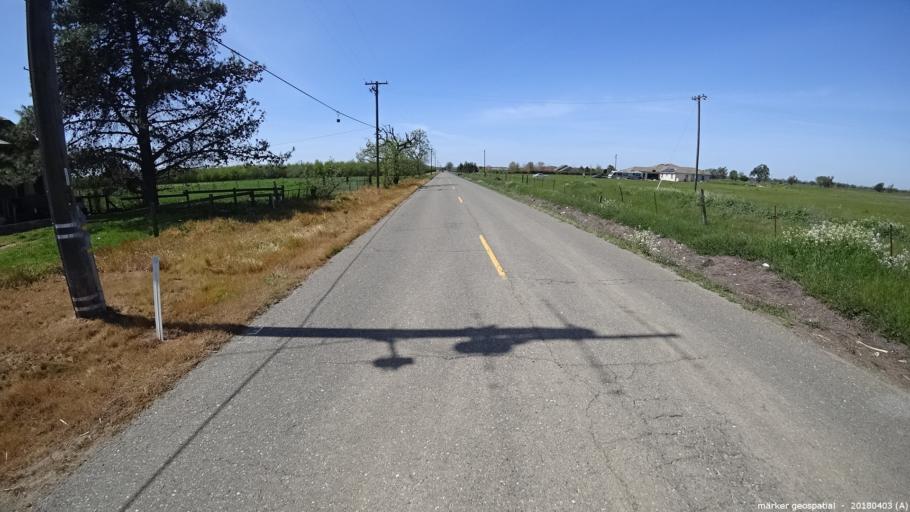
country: US
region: California
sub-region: Sacramento County
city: Wilton
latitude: 38.3799
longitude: -121.2824
